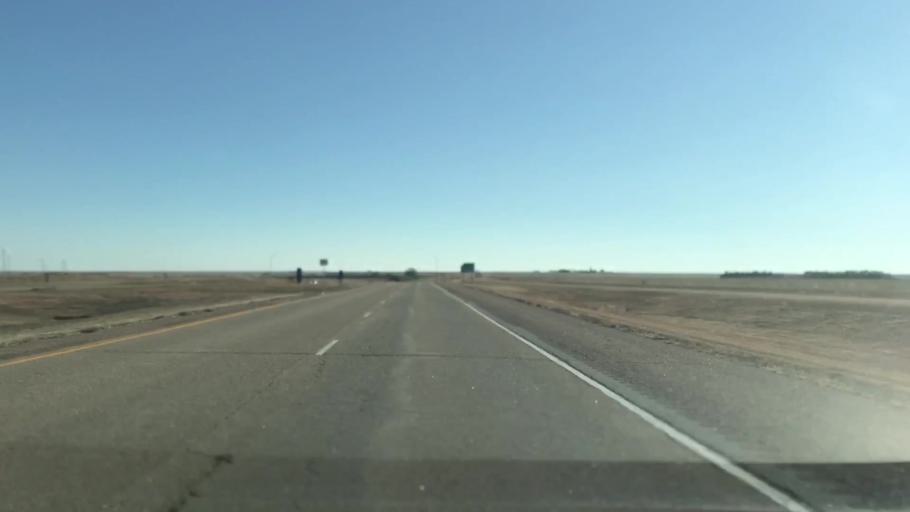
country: US
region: Colorado
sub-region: Lincoln County
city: Hugo
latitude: 39.2786
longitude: -103.4059
